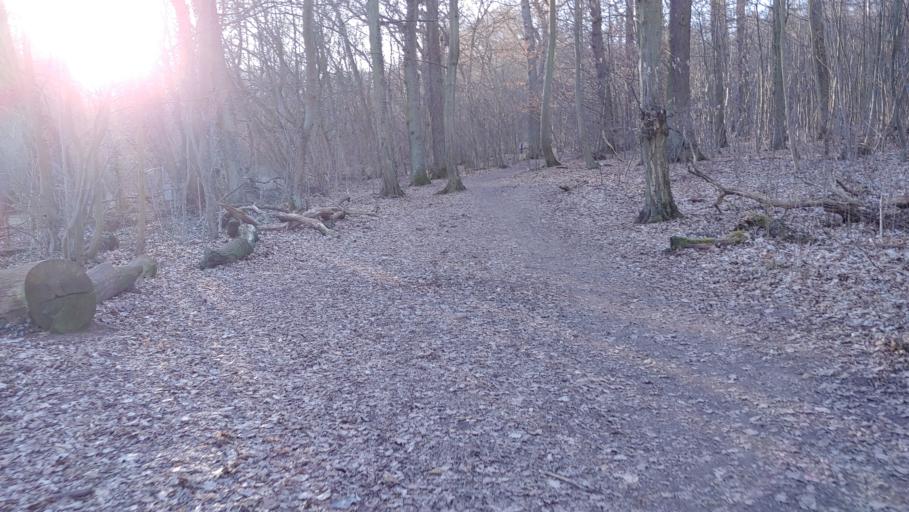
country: DE
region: Hesse
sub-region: Regierungsbezirk Kassel
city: Vellmar
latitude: 51.3275
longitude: 9.4281
